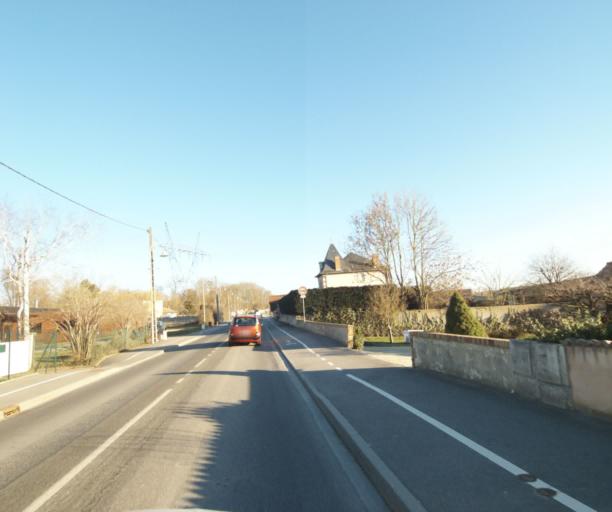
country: FR
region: Lorraine
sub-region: Departement de Meurthe-et-Moselle
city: Art-sur-Meurthe
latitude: 48.6586
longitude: 6.2606
